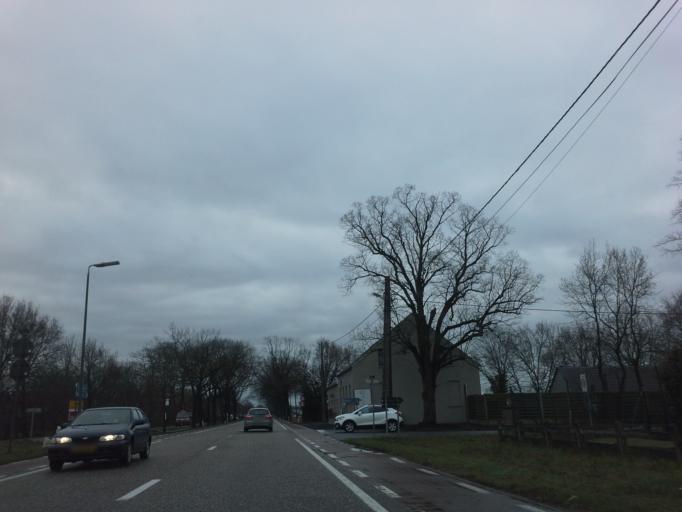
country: BE
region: Flanders
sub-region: Provincie Limburg
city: Leopoldsburg
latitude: 51.1544
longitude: 5.2615
